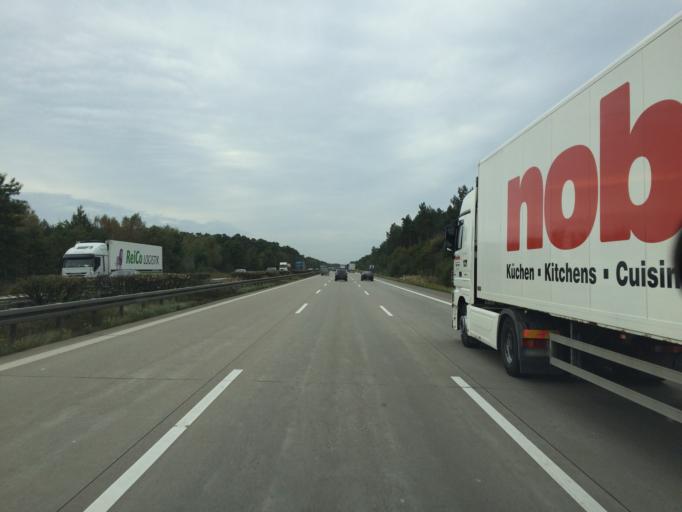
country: DE
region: Brandenburg
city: Wollin
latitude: 52.3287
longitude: 12.4997
